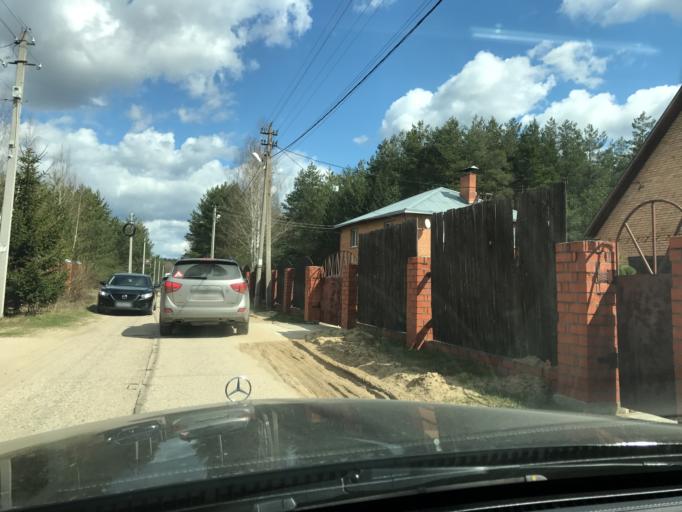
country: RU
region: Vladimir
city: Pokrov
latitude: 55.8578
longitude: 39.2024
